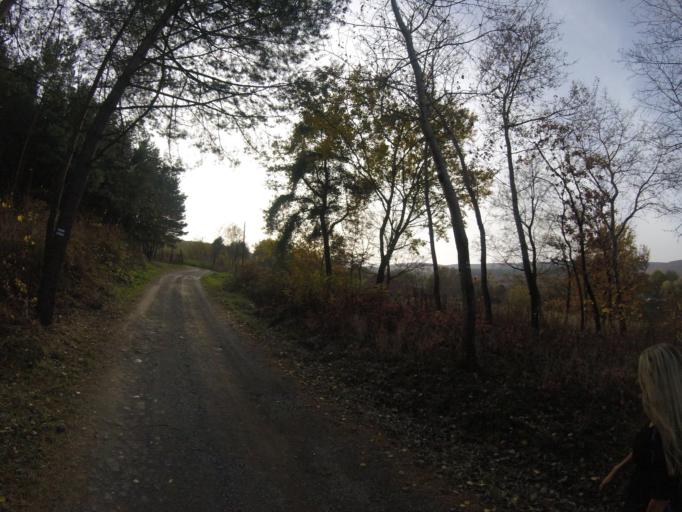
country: HU
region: Borsod-Abauj-Zemplen
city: Gonc
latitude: 48.5095
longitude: 21.4552
